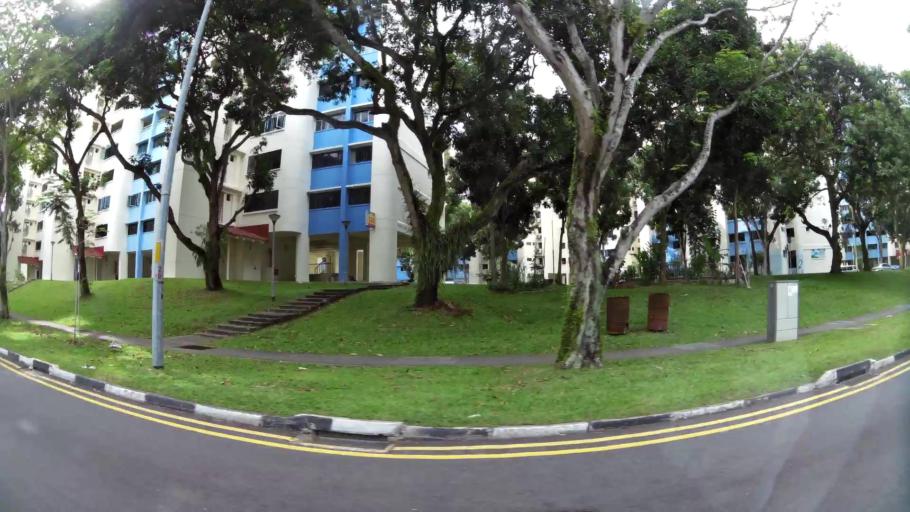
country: SG
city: Singapore
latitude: 1.3667
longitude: 103.8989
